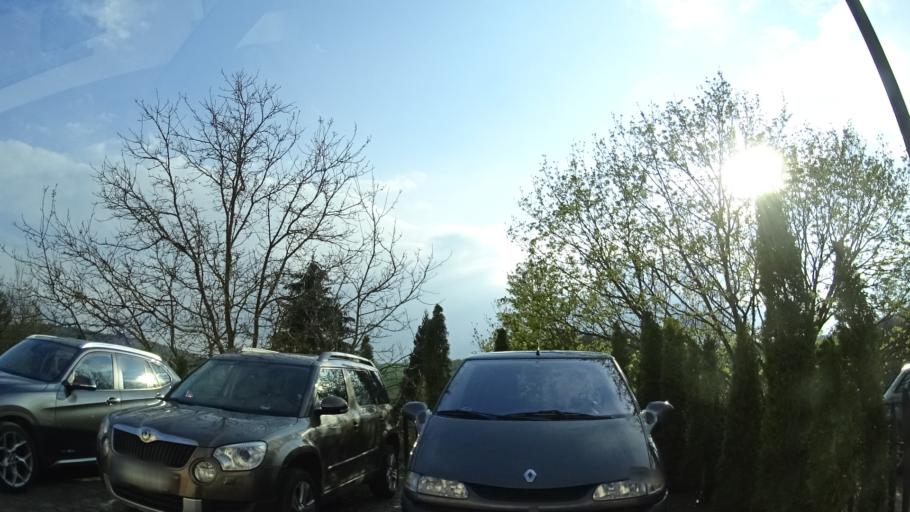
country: DE
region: Rheinland-Pfalz
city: Sponheim
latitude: 49.8447
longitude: 7.7244
